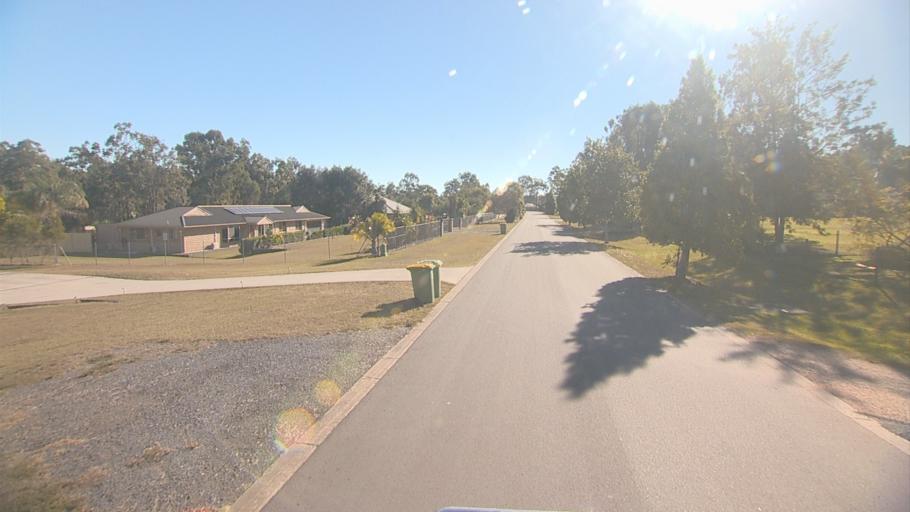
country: AU
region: Queensland
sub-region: Logan
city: North Maclean
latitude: -27.7350
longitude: 152.9680
